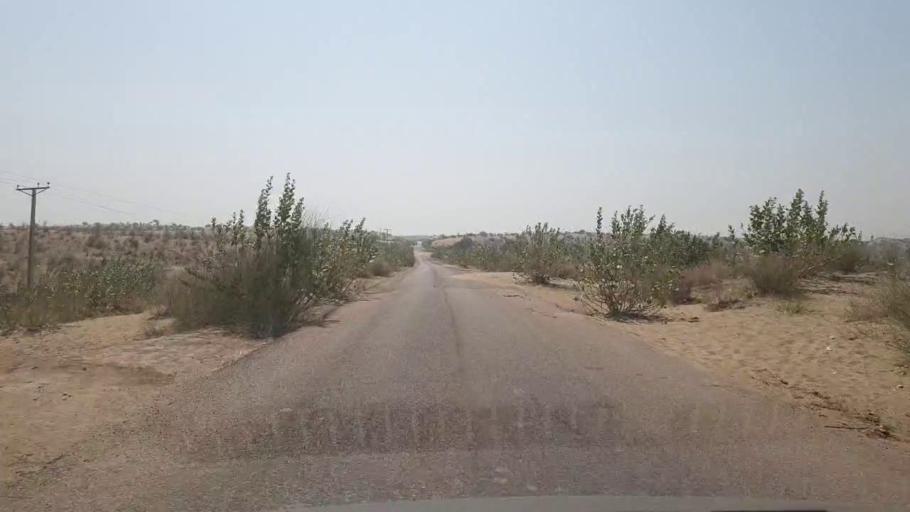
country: PK
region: Sindh
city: Chor
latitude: 25.6619
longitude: 70.1669
